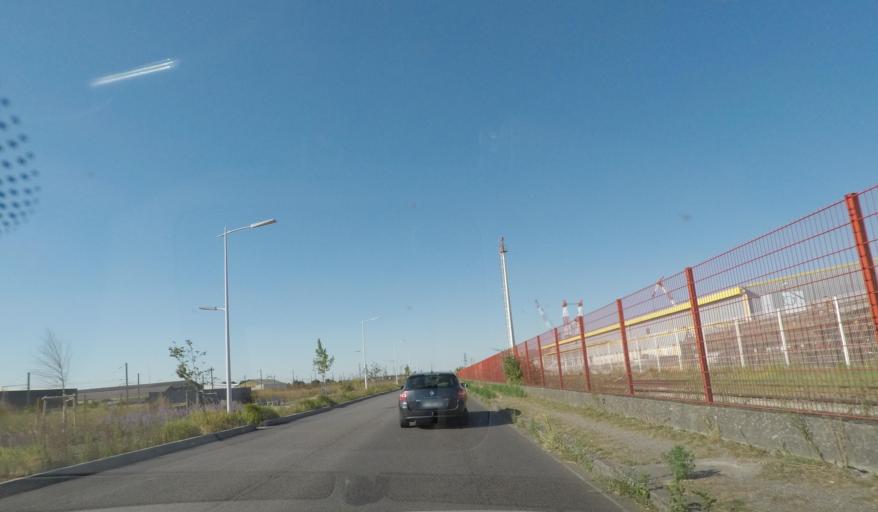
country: FR
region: Pays de la Loire
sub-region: Departement de la Loire-Atlantique
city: Saint-Nazaire
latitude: 47.2850
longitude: -2.2013
